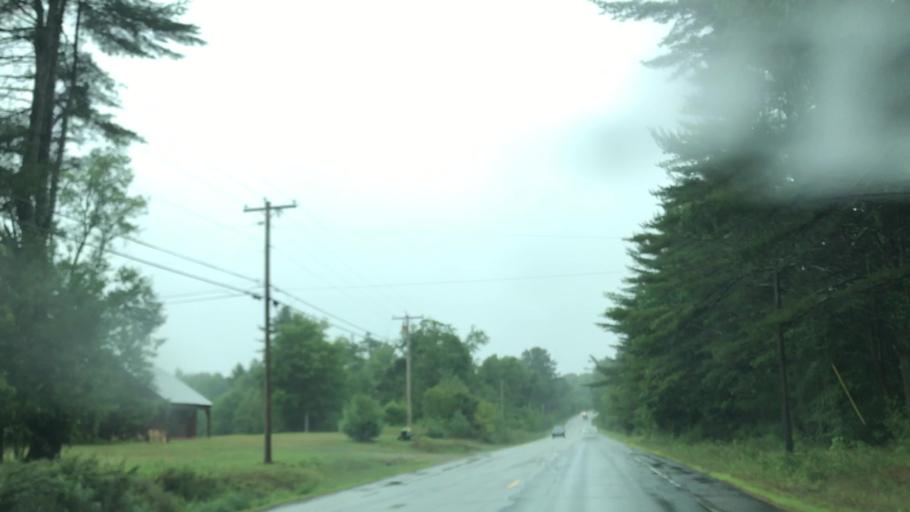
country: US
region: Maine
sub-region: York County
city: North Berwick
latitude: 43.2993
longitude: -70.7709
